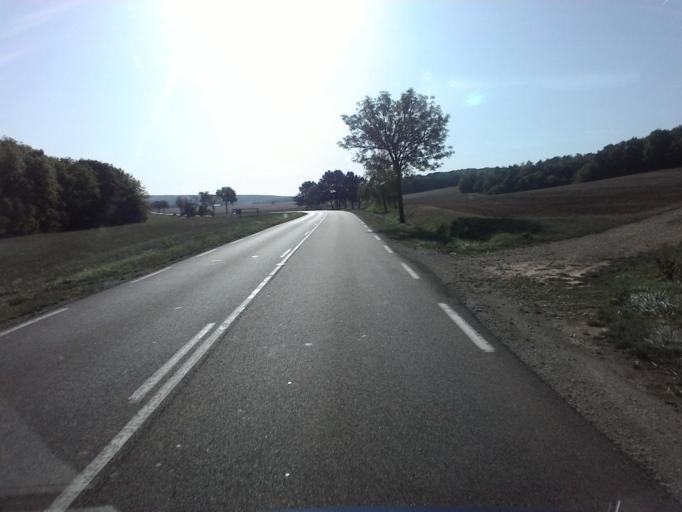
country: FR
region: Champagne-Ardenne
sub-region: Departement de l'Aube
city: Bar-sur-Seine
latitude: 48.1304
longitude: 4.3392
